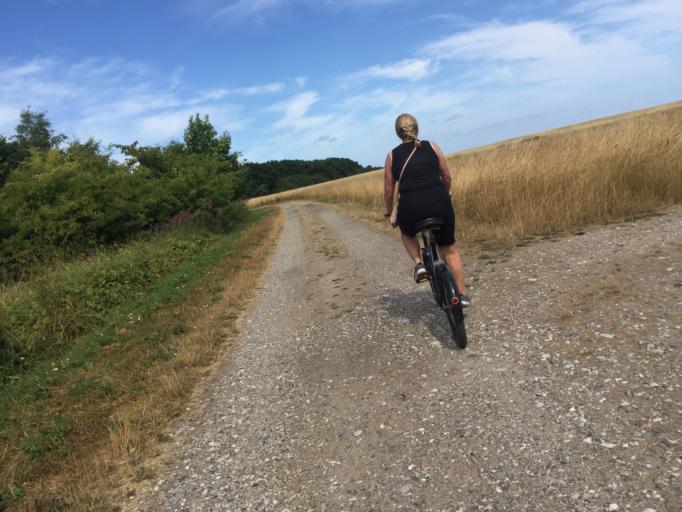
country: DK
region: Central Jutland
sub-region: Arhus Kommune
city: Beder
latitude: 55.9580
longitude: 10.4111
